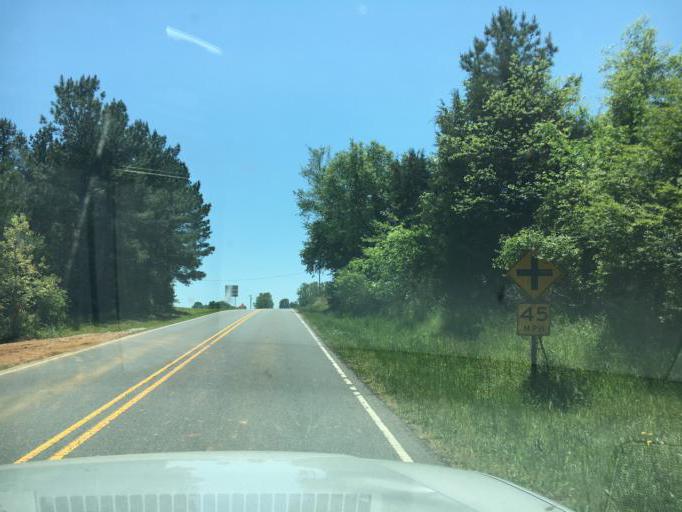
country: US
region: South Carolina
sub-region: Cherokee County
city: Blacksburg
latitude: 35.1826
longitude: -81.5710
